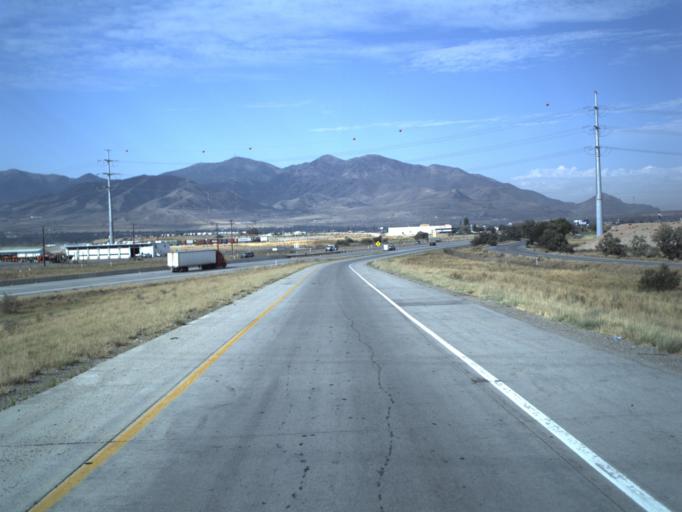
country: US
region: Utah
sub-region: Salt Lake County
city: West Valley City
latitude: 40.7267
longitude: -112.0259
